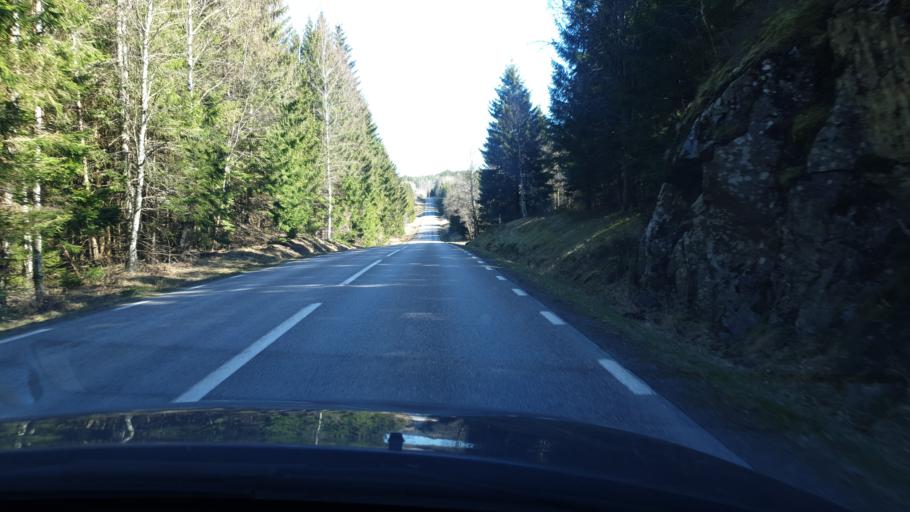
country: SE
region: Vaestra Goetaland
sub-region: Tanums Kommun
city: Tanumshede
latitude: 58.7450
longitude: 11.4966
